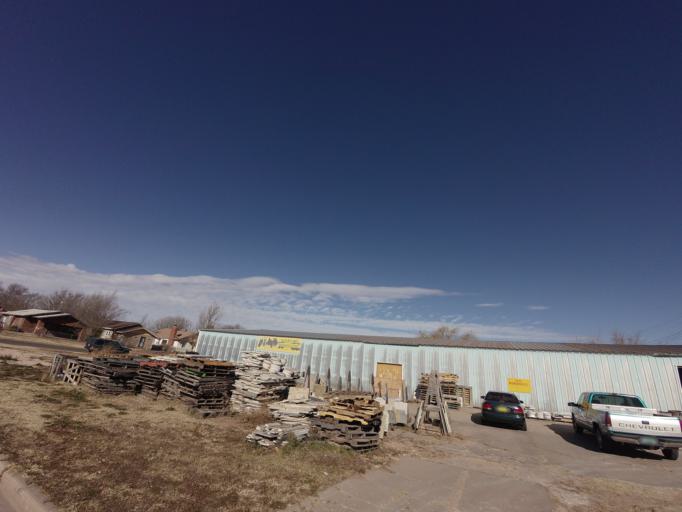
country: US
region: New Mexico
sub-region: Curry County
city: Clovis
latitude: 34.4029
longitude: -103.2075
